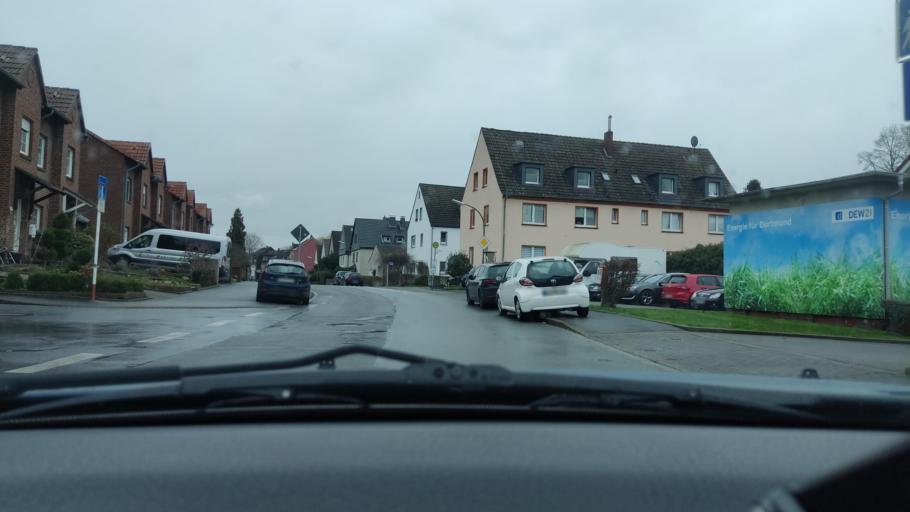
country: DE
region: North Rhine-Westphalia
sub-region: Regierungsbezirk Arnsberg
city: Dortmund
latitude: 51.5548
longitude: 7.4482
